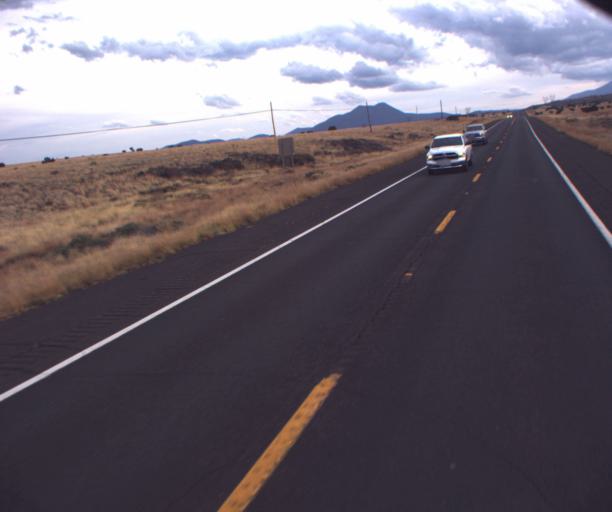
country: US
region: Arizona
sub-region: Coconino County
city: Flagstaff
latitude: 35.5535
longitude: -111.5361
